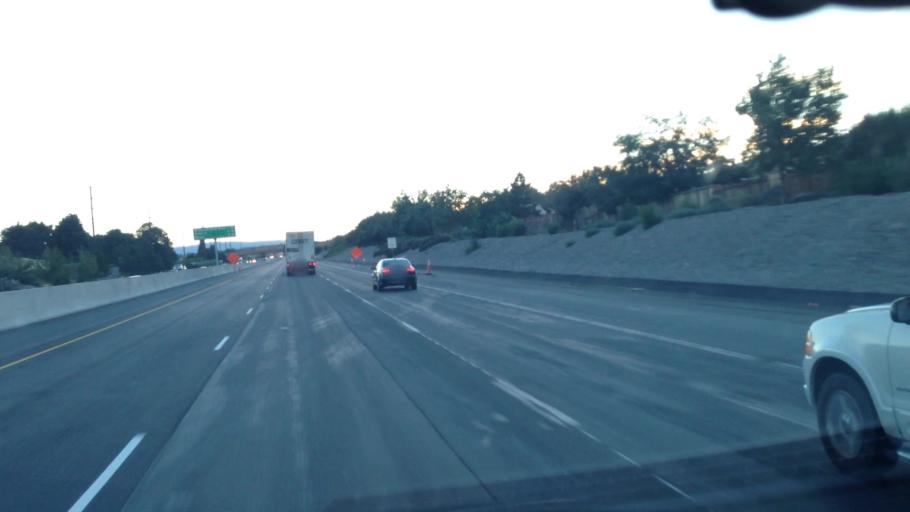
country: US
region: Nevada
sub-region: Washoe County
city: Reno
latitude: 39.5272
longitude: -119.8393
